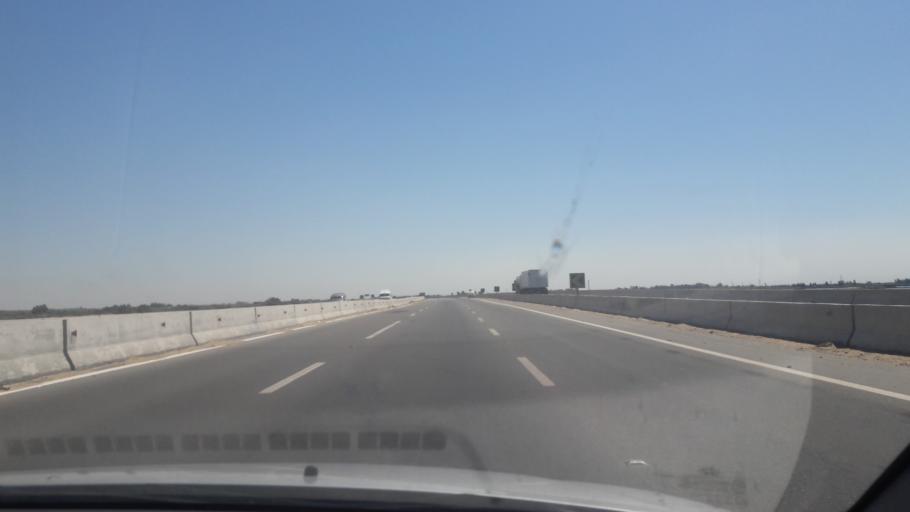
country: EG
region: Al Isma'iliyah
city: Ismailia
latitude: 30.9036
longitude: 32.1826
